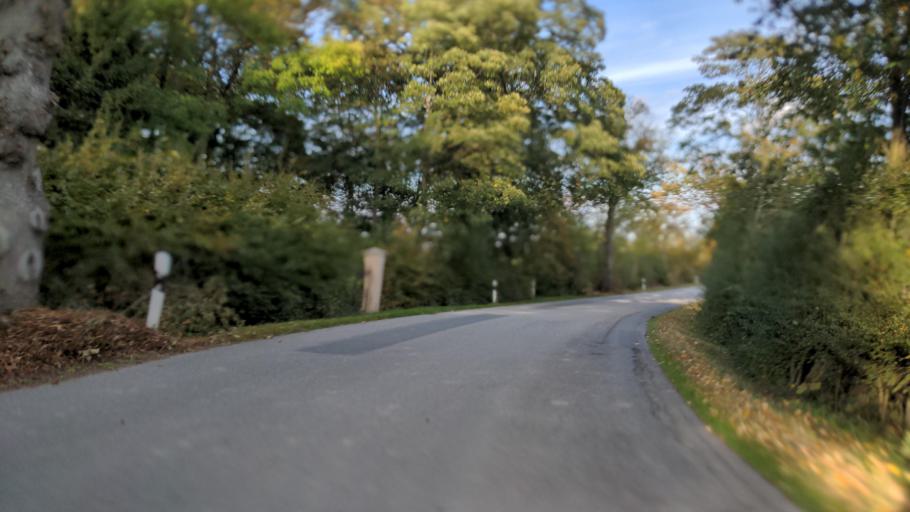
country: DE
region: Schleswig-Holstein
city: Ahrensbok
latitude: 53.9907
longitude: 10.5737
